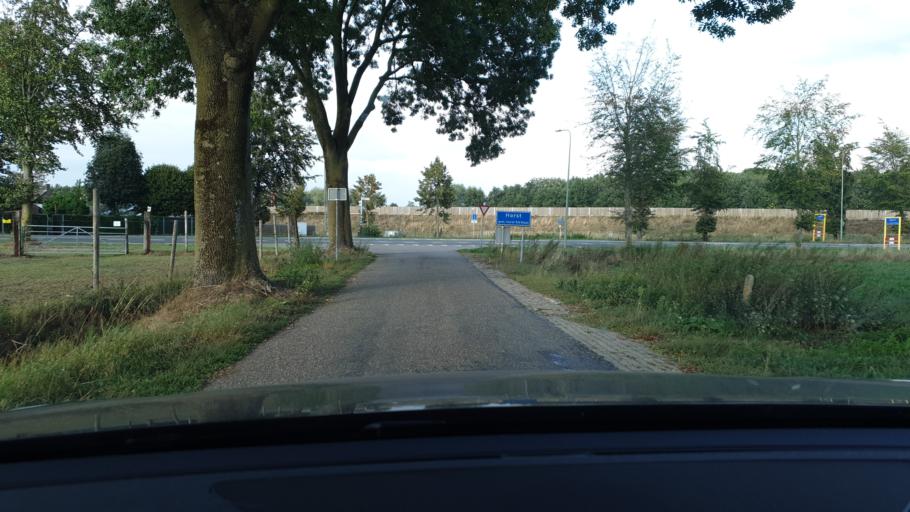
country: NL
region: Limburg
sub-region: Gemeente Peel en Maas
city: Maasbree
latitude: 51.4467
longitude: 6.0684
